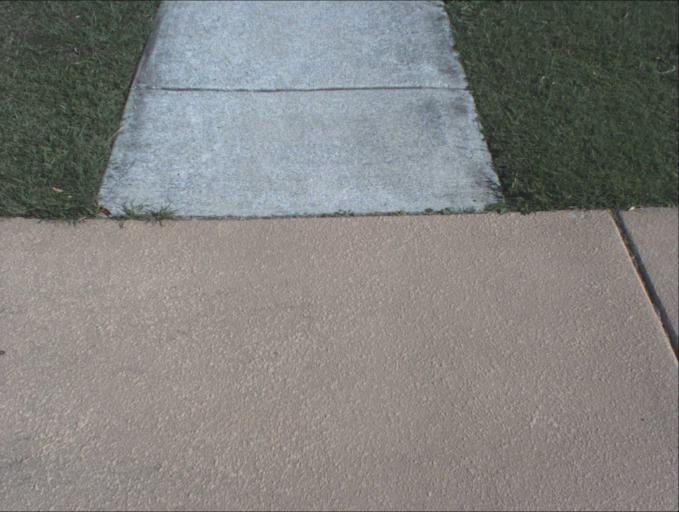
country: AU
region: Queensland
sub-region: Logan
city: Logan City
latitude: -27.6696
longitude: 153.0929
